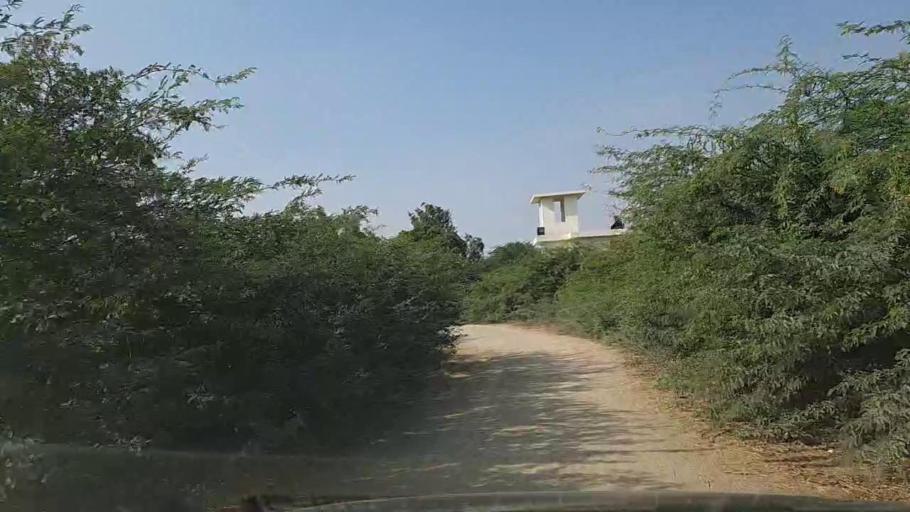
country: PK
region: Sindh
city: Gharo
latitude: 24.7716
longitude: 67.5694
